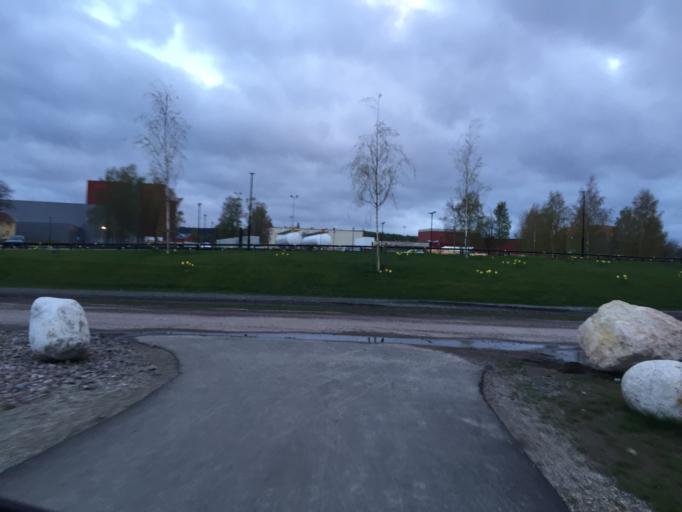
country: SE
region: Dalarna
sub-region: Ludvika Kommun
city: Ludvika
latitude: 60.1484
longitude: 15.1796
